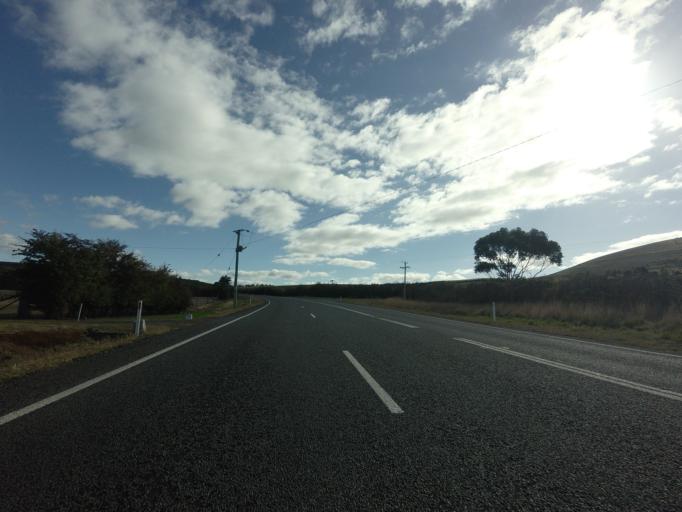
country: AU
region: Tasmania
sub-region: Derwent Valley
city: New Norfolk
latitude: -42.7183
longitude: 146.9481
